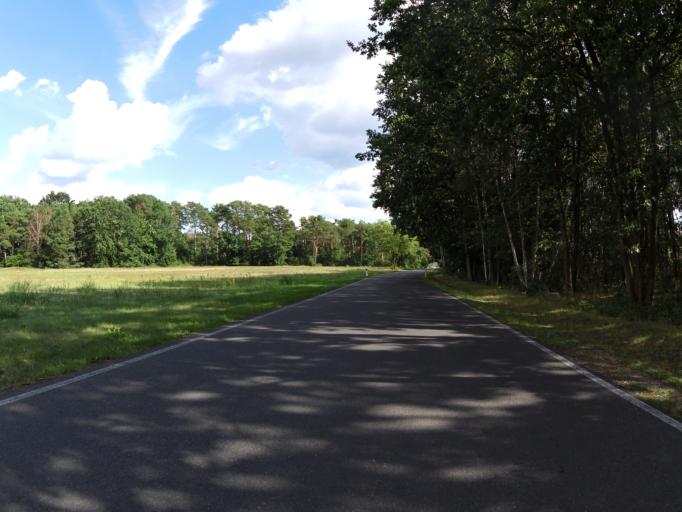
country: DE
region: Brandenburg
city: Munchehofe
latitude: 52.1951
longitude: 13.8685
